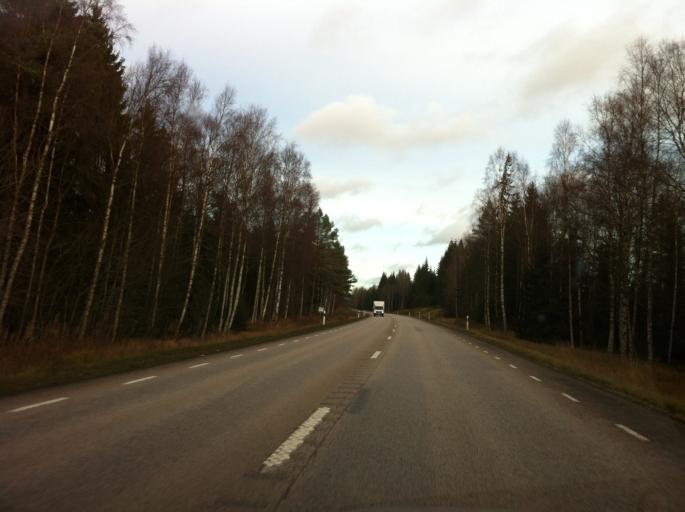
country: SE
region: Kronoberg
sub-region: Uppvidinge Kommun
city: Aseda
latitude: 57.1207
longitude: 15.2470
